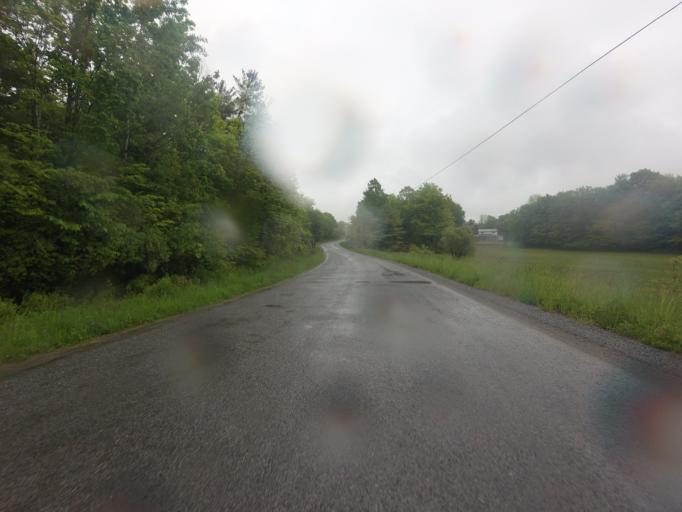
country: CA
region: Ontario
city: Kingston
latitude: 44.4821
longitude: -76.4605
